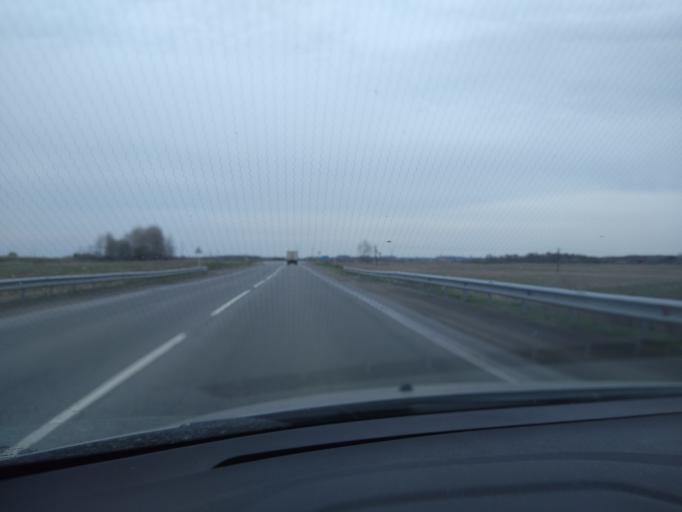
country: RU
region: Sverdlovsk
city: Kamyshlov
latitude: 56.8760
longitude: 62.7054
